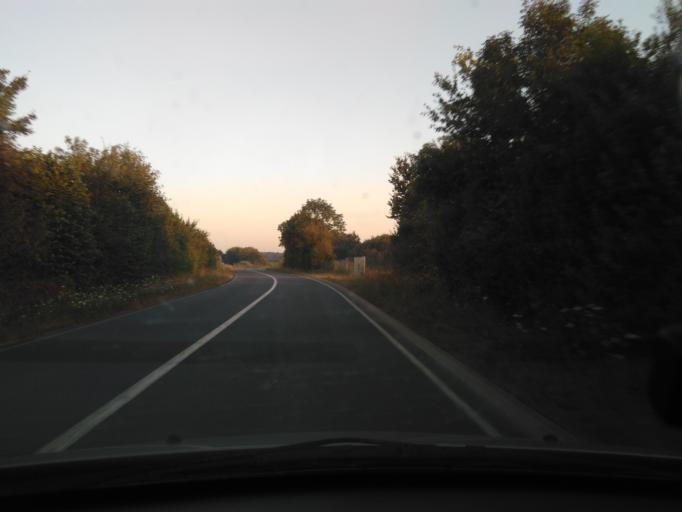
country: FR
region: Pays de la Loire
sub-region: Departement de la Vendee
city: Chauche
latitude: 46.8356
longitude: -1.2765
